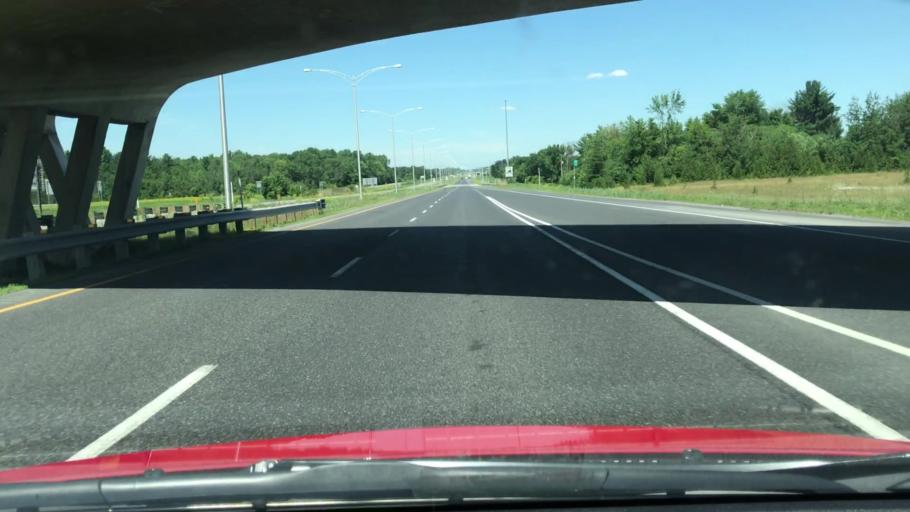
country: US
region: New York
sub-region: Clinton County
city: Champlain
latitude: 45.0199
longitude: -73.4528
